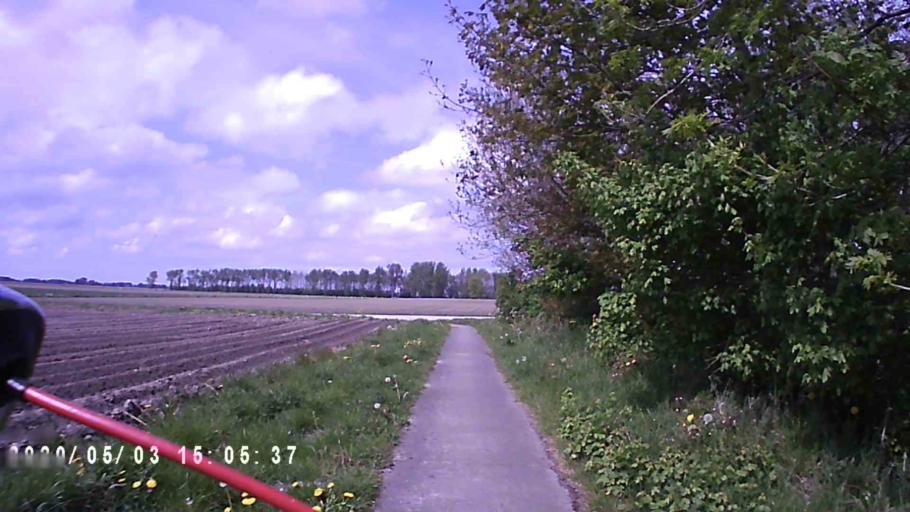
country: NL
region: Groningen
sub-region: Gemeente Zuidhorn
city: Oldehove
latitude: 53.3712
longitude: 6.4416
